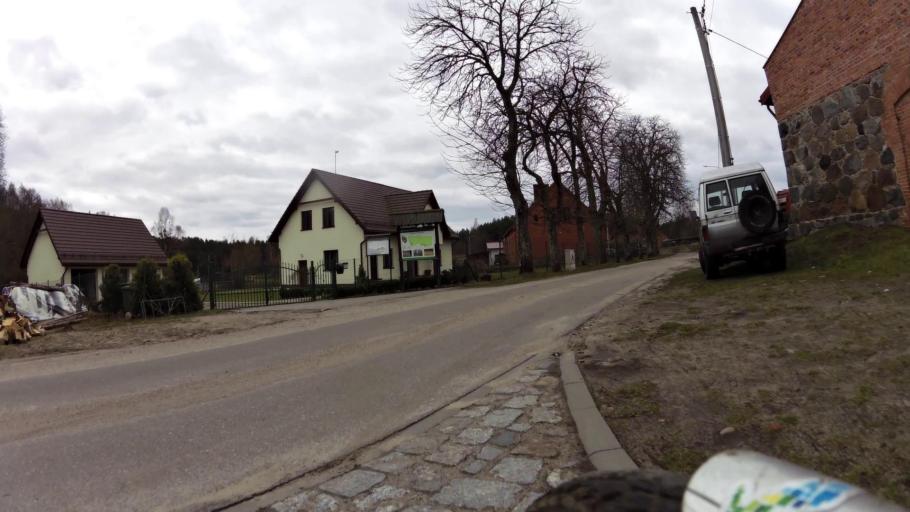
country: PL
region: Pomeranian Voivodeship
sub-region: Powiat bytowski
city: Trzebielino
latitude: 54.1397
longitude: 17.1494
